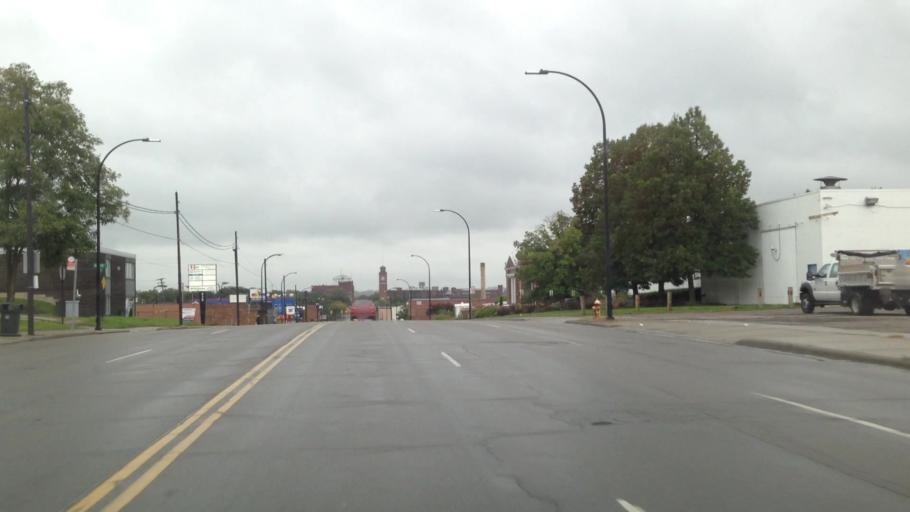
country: US
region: Ohio
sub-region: Summit County
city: Akron
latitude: 41.0742
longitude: -81.4929
